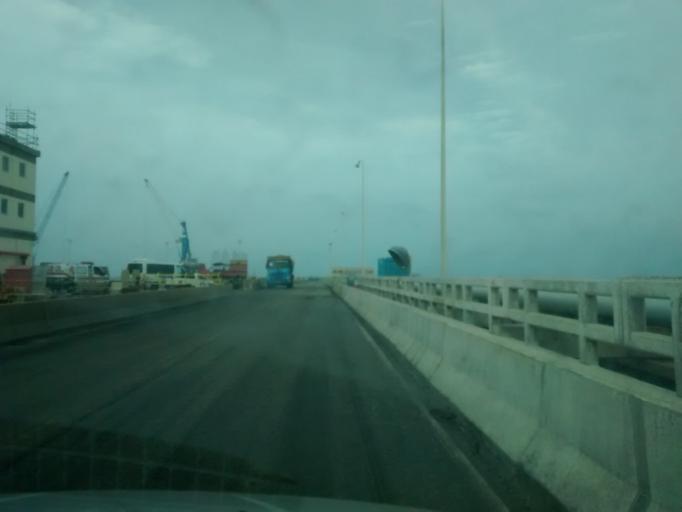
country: BR
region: Ceara
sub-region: Caucaia
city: Cambebba
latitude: -3.5337
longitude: -38.7964
